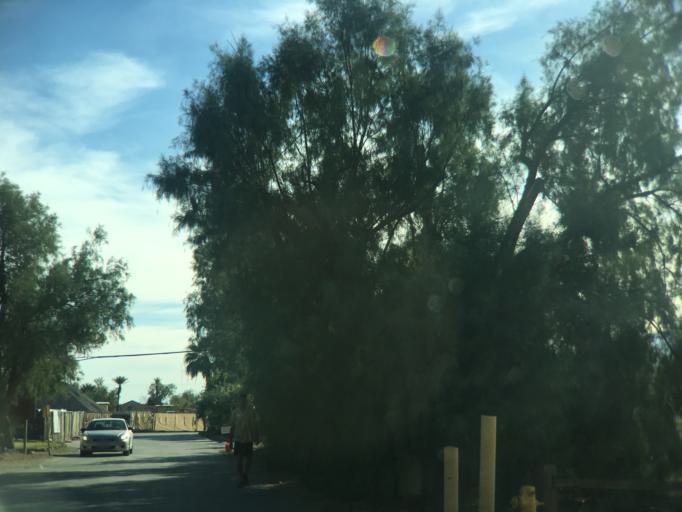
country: US
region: Nevada
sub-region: Nye County
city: Beatty
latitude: 36.4578
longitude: -116.8665
